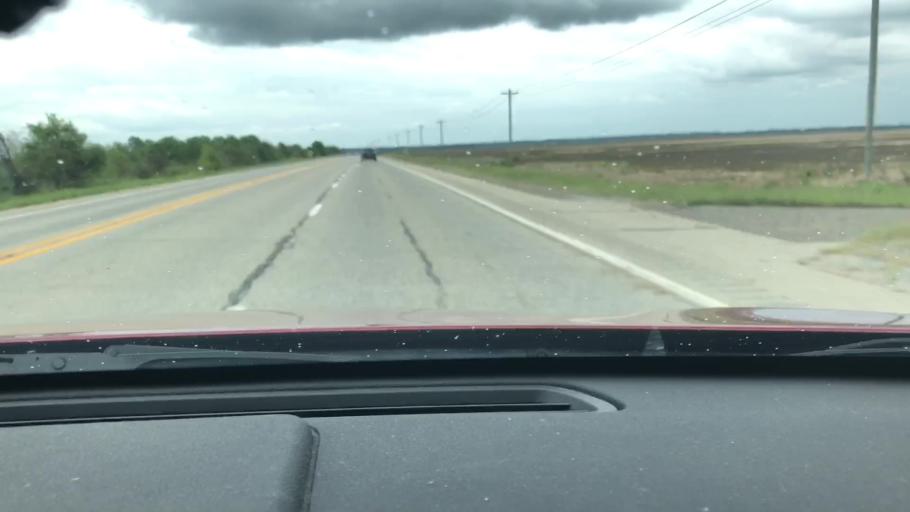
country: US
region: Arkansas
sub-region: Lafayette County
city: Lewisville
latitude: 33.4123
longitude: -93.7871
